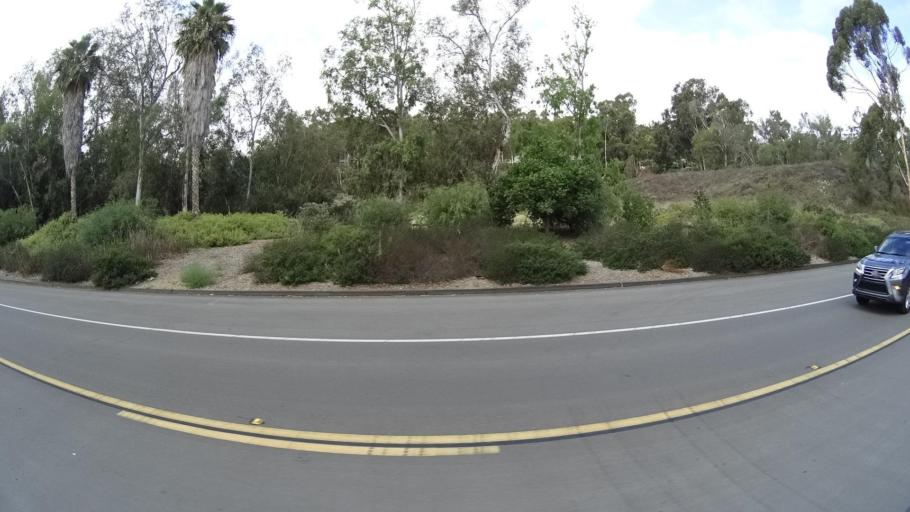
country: US
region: California
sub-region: San Diego County
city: Fairbanks Ranch
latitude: 32.9860
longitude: -117.2170
